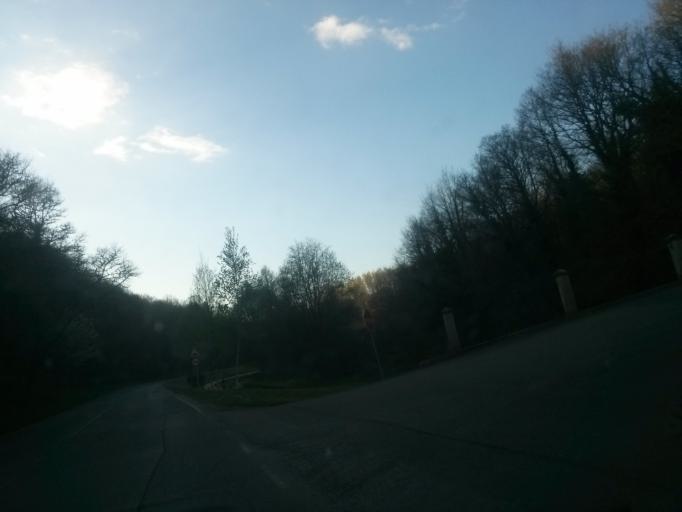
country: ES
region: Galicia
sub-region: Provincia de Lugo
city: Lugo
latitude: 43.0043
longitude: -7.5342
